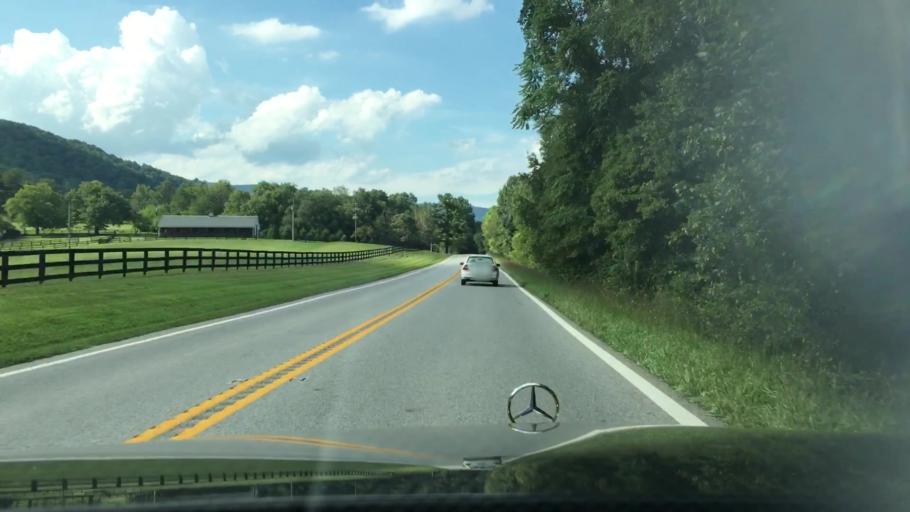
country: US
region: Virginia
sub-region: Nelson County
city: Nellysford
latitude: 37.9583
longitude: -78.8331
